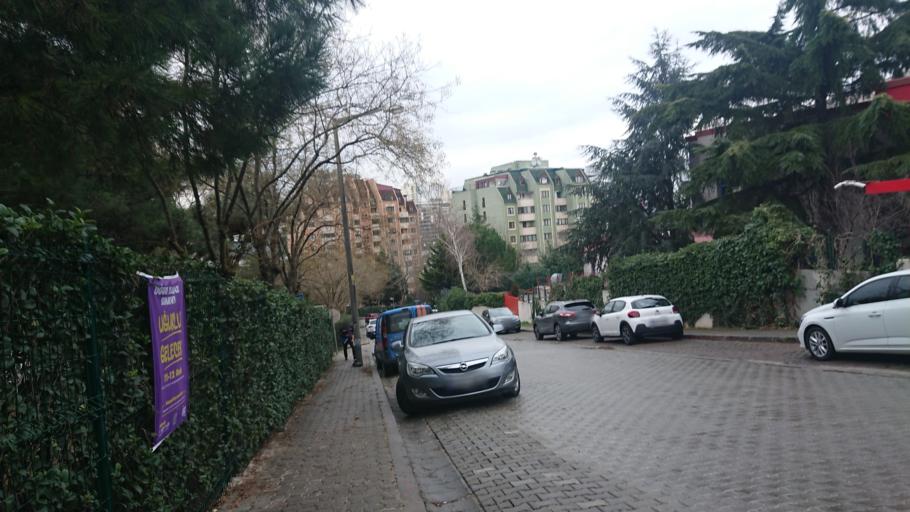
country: TR
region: Istanbul
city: Esenyurt
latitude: 41.0662
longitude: 28.6859
